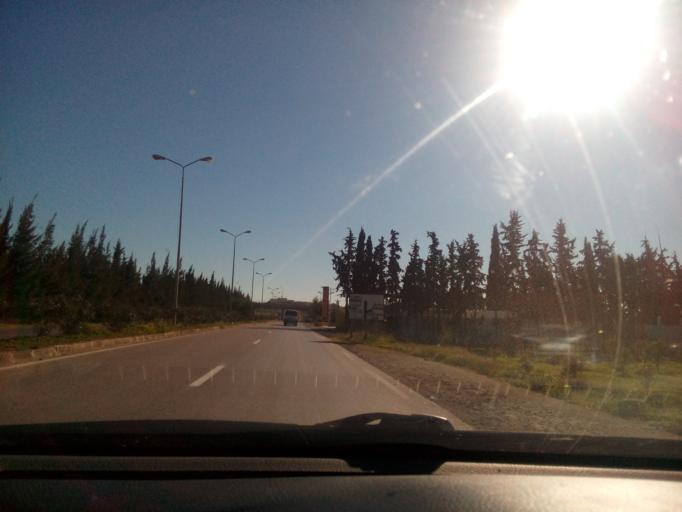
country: DZ
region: Relizane
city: Relizane
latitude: 35.7192
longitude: 0.5075
